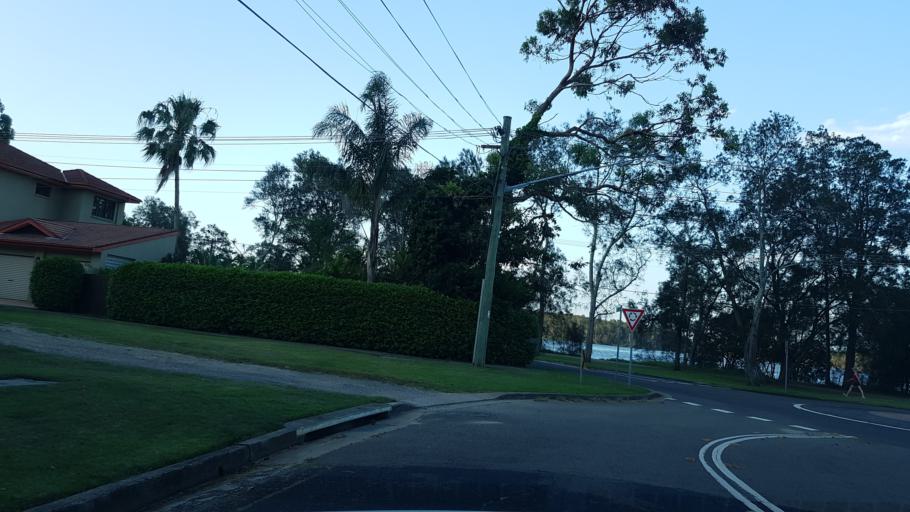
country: AU
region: New South Wales
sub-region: Warringah
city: Narrabeen
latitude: -33.7216
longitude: 151.2919
